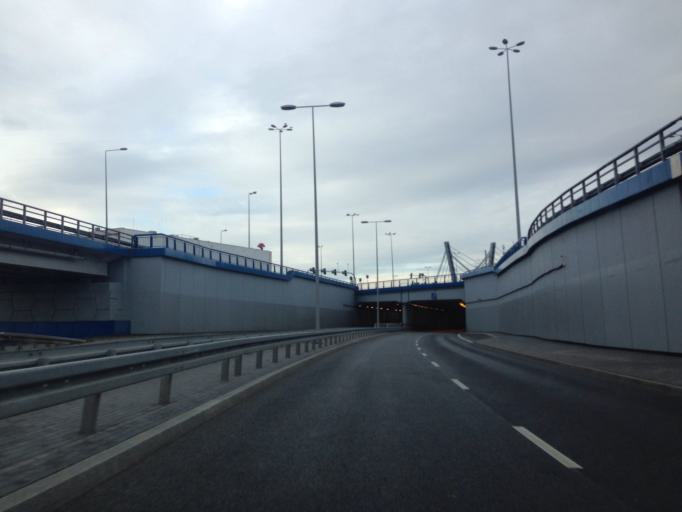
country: PL
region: Kujawsko-Pomorskie
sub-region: Torun
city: Torun
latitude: 53.0205
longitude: 18.6495
